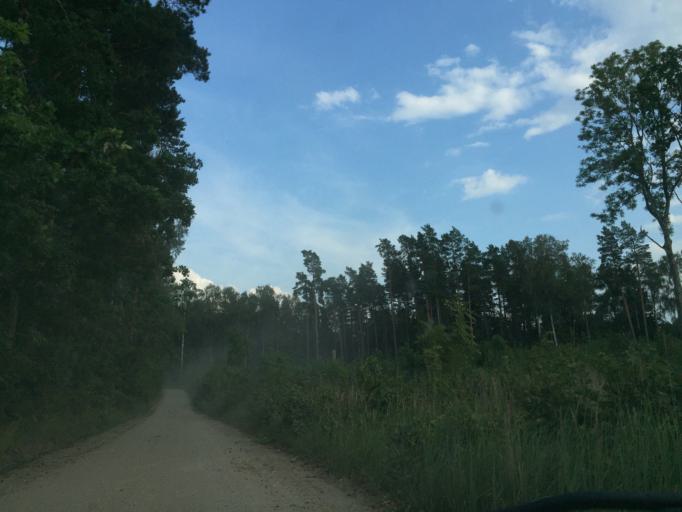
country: LT
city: Zagare
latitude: 56.4470
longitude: 23.1548
